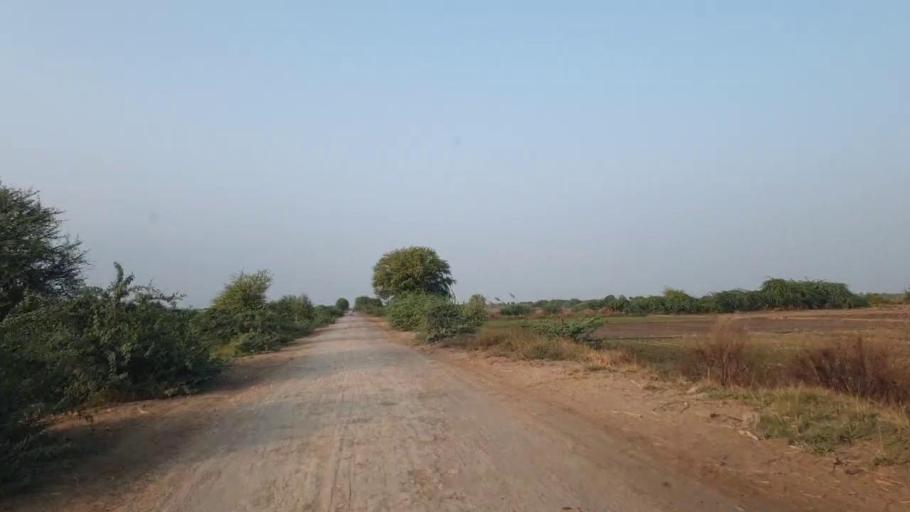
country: PK
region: Sindh
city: Tando Ghulam Ali
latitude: 25.0702
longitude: 68.9595
